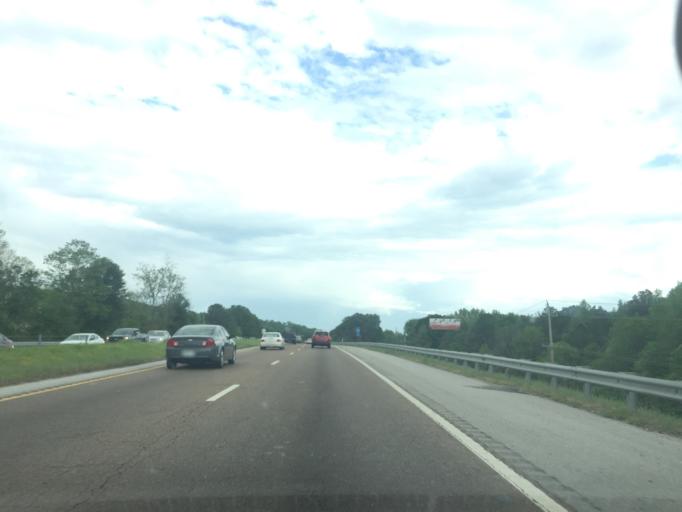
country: US
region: Tennessee
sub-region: Hamilton County
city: East Chattanooga
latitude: 35.1189
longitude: -85.2358
